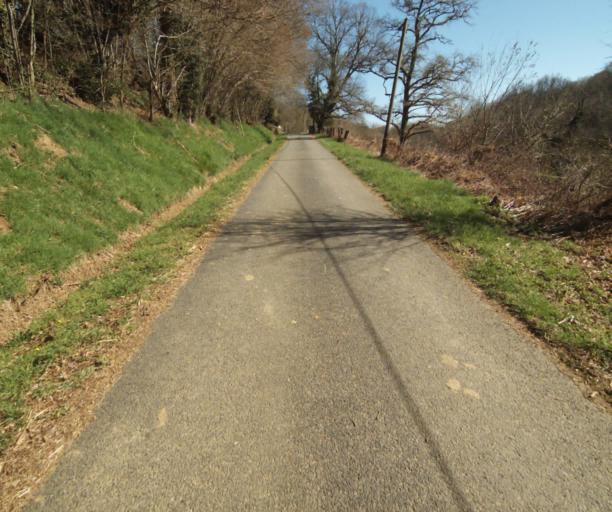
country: FR
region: Limousin
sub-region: Departement de la Correze
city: Uzerche
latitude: 45.4085
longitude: 1.6335
